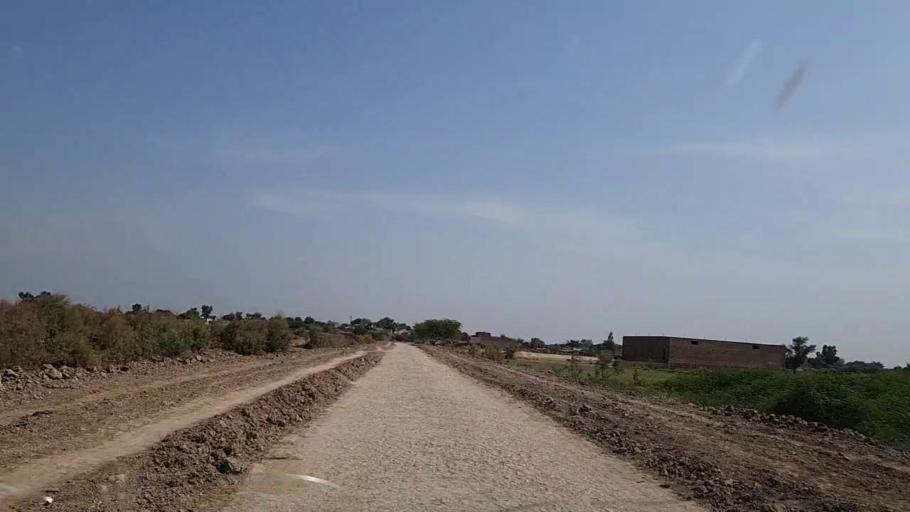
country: PK
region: Sindh
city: Khanpur
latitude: 27.7533
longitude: 69.3371
